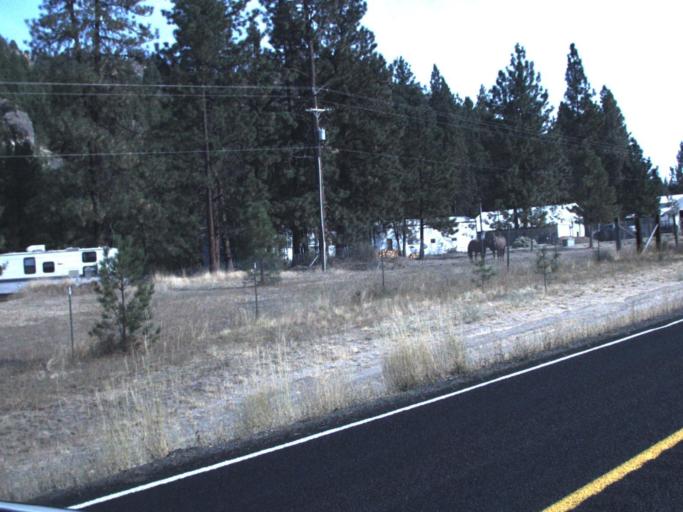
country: US
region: Washington
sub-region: Spokane County
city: Fairchild Air Force Base
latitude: 47.8411
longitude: -117.7425
